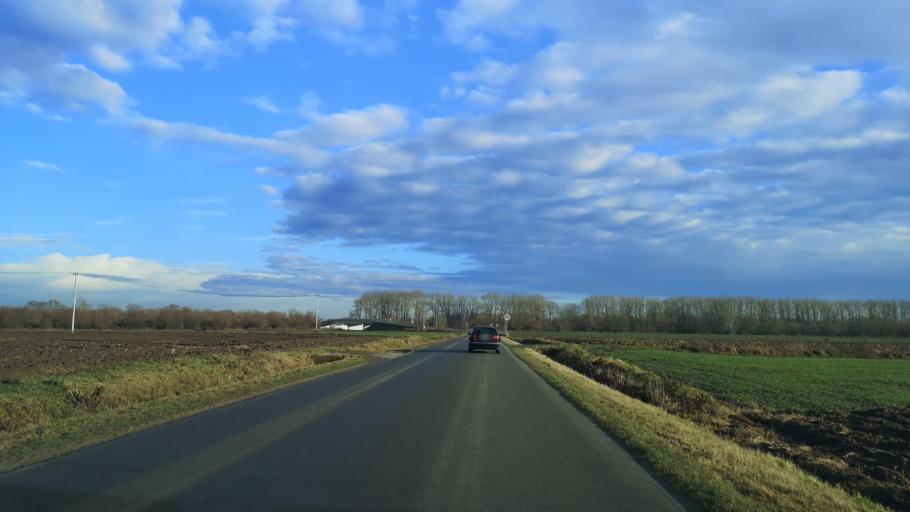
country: PL
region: Subcarpathian Voivodeship
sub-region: Powiat lezajski
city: Piskorowice
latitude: 50.2466
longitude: 22.4942
